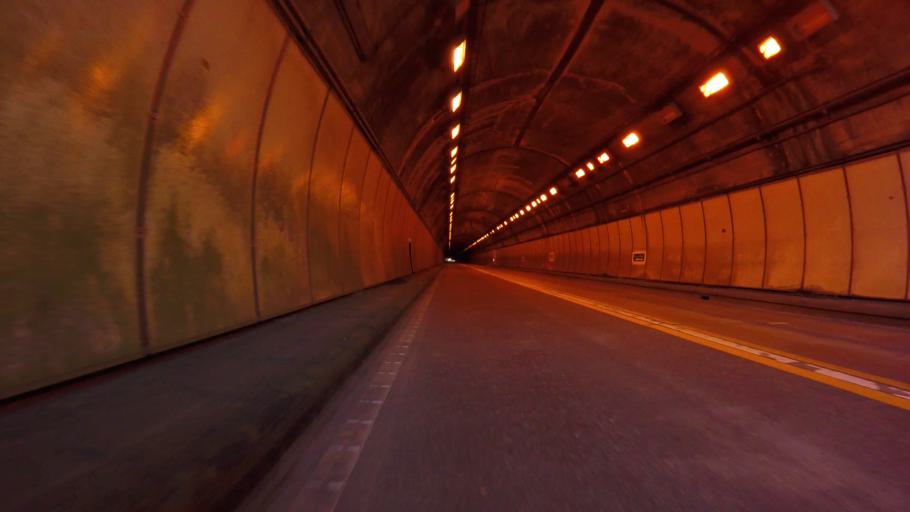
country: JP
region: Shizuoka
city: Atami
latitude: 35.1102
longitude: 139.0422
